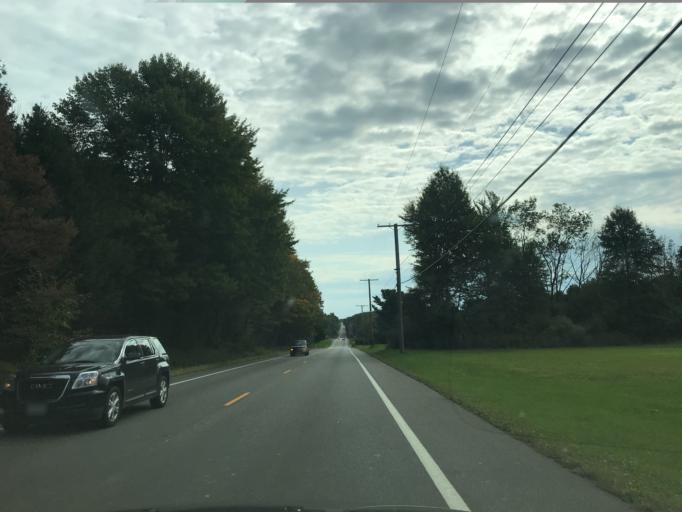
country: US
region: Ohio
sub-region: Portage County
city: Hiram
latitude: 41.3848
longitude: -81.1335
